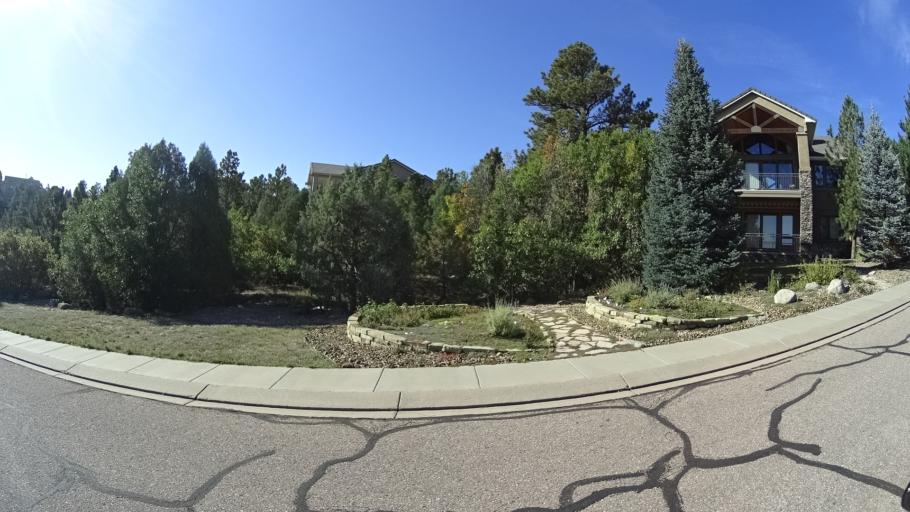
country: US
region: Colorado
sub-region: El Paso County
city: Colorado Springs
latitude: 38.9028
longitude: -104.7947
